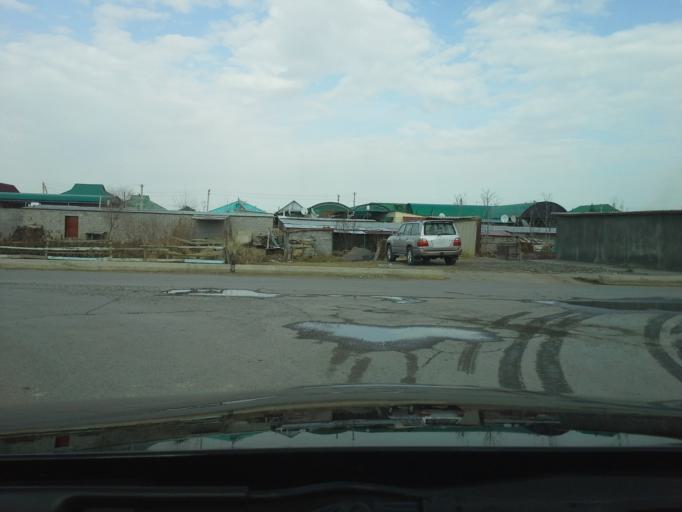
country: TM
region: Ahal
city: Abadan
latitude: 37.9919
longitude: 58.2841
